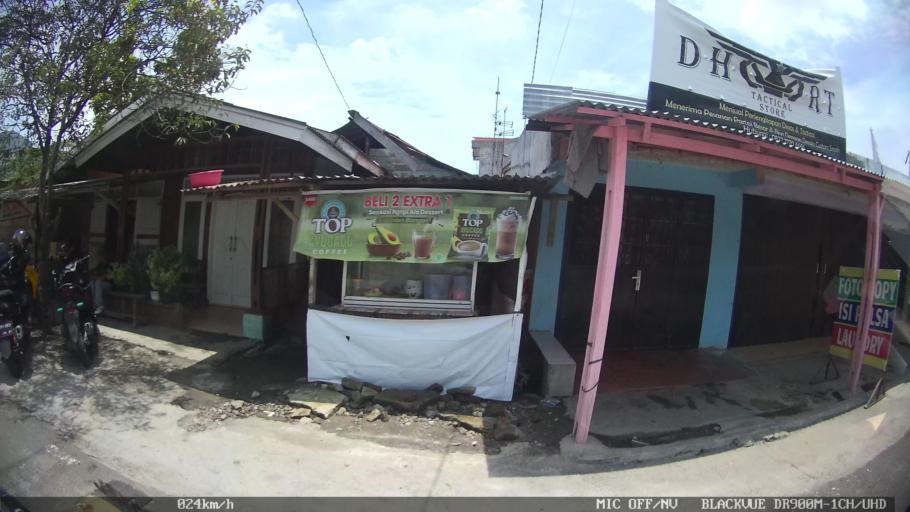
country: ID
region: North Sumatra
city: Percut
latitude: 3.5594
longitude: 98.8606
